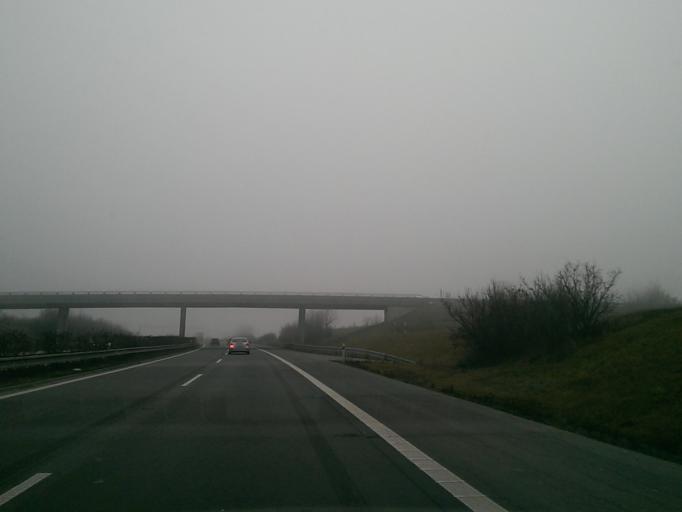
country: CZ
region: Olomoucky
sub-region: Okres Olomouc
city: Olomouc
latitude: 49.5528
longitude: 17.2286
